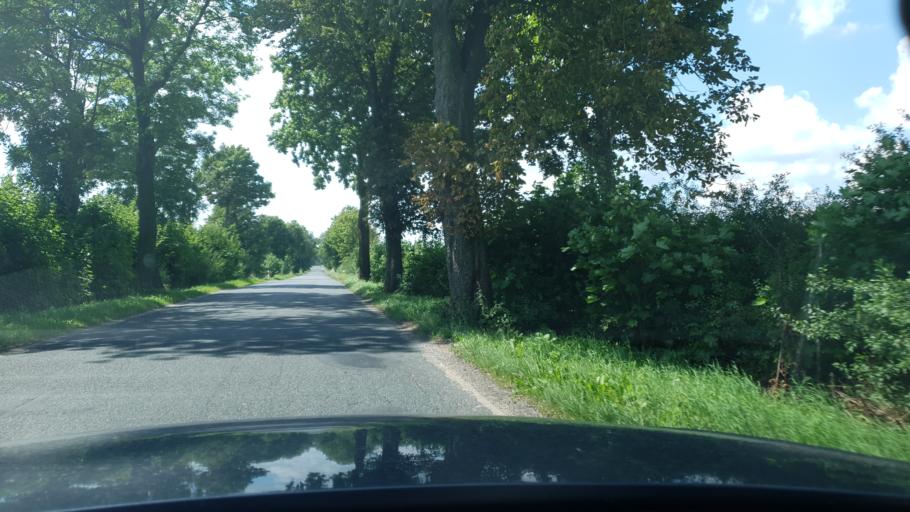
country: PL
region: Kujawsko-Pomorskie
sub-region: Powiat wabrzeski
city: Pluznica
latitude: 53.3766
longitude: 18.8245
